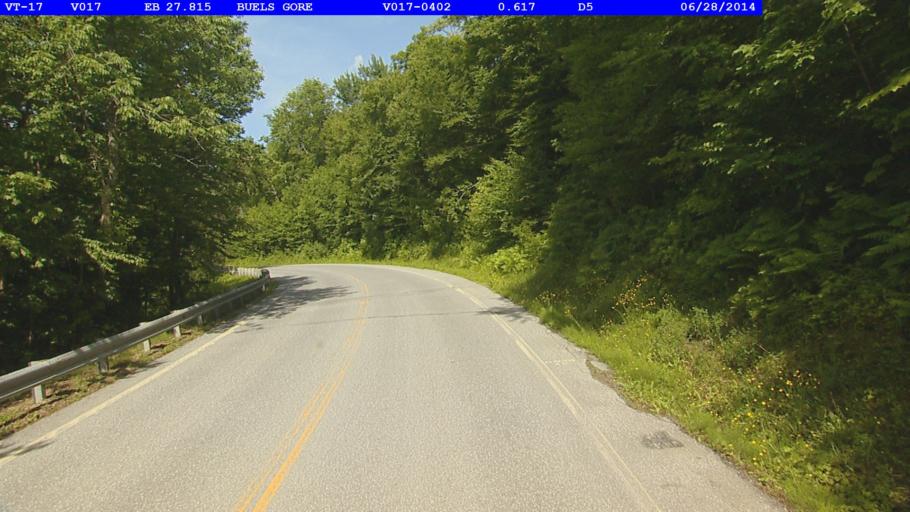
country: US
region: Vermont
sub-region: Addison County
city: Bristol
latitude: 44.2174
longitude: -72.9555
